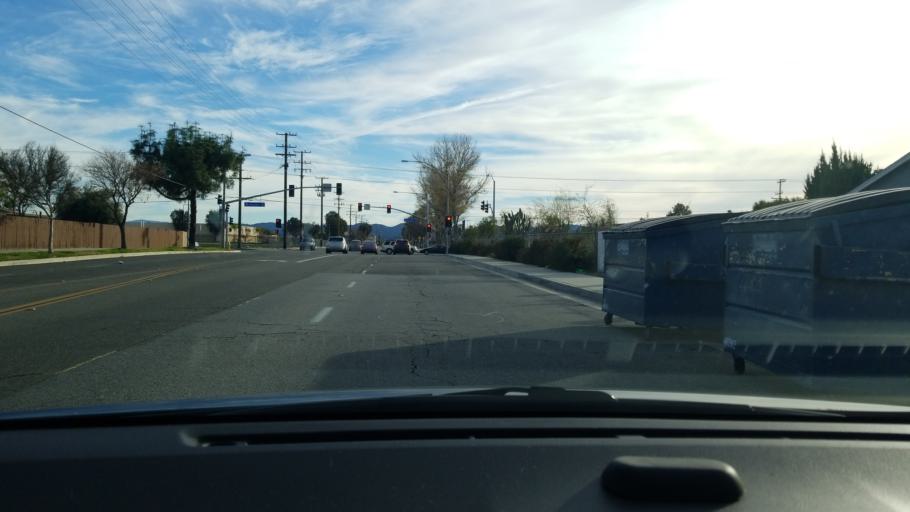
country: US
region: California
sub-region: Riverside County
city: Hemet
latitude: 33.7519
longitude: -116.9979
